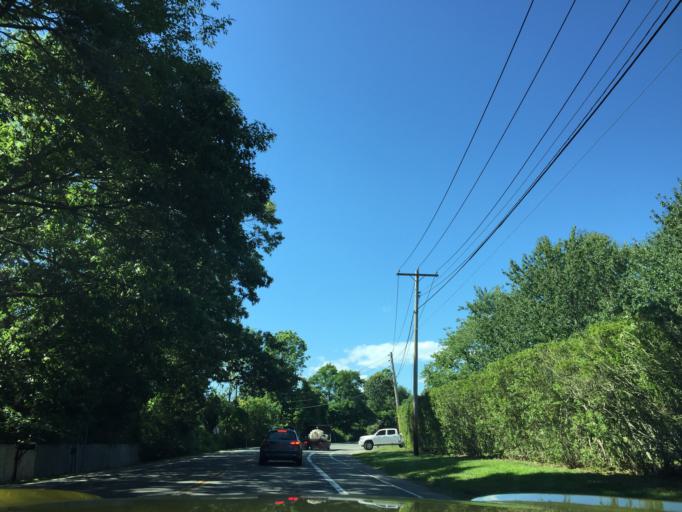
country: US
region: New York
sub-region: Suffolk County
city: Sag Harbor
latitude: 41.0254
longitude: -72.3118
